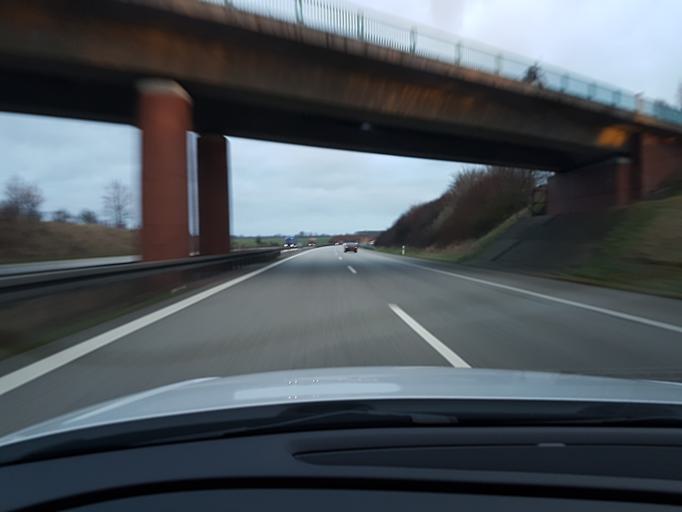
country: DE
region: Mecklenburg-Vorpommern
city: Muhlen Eichsen
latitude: 53.8283
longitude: 11.2756
